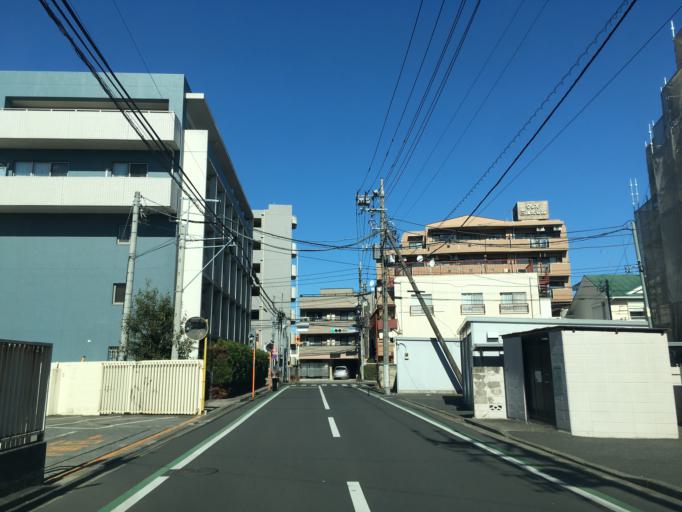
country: JP
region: Tokyo
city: Mitaka-shi
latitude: 35.6831
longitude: 139.5610
